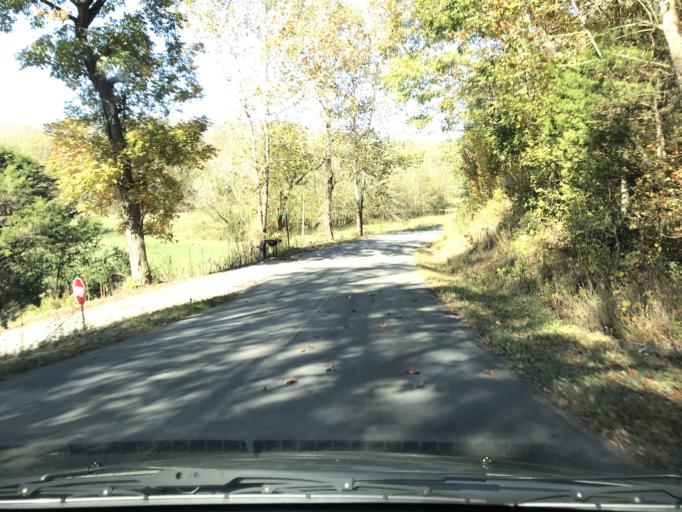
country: US
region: Georgia
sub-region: Dade County
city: Trenton
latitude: 34.9087
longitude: -85.4715
